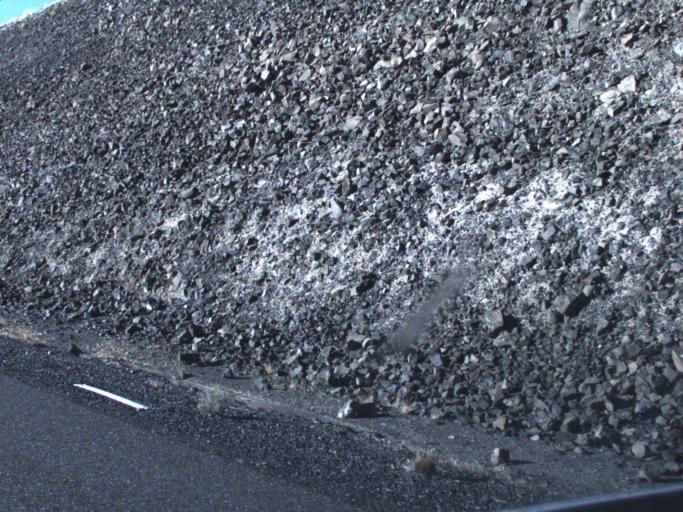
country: US
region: Washington
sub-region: Benton County
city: Highland
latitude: 46.1339
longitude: -119.0901
